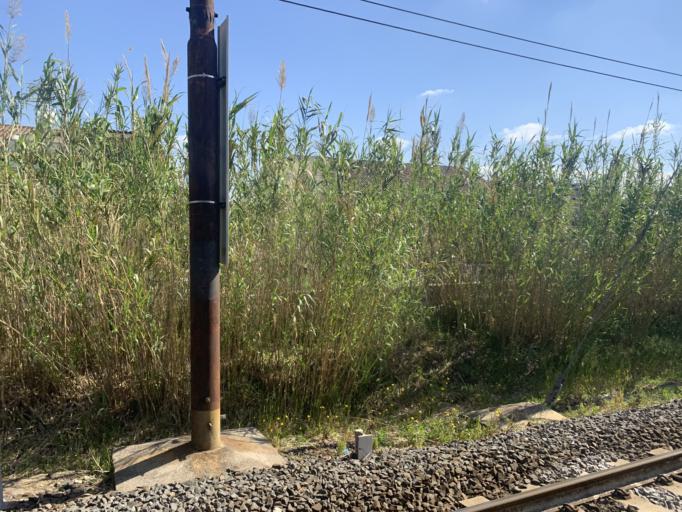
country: IT
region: Latium
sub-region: Citta metropolitana di Roma Capitale
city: Ciampino
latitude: 41.8066
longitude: 12.5940
